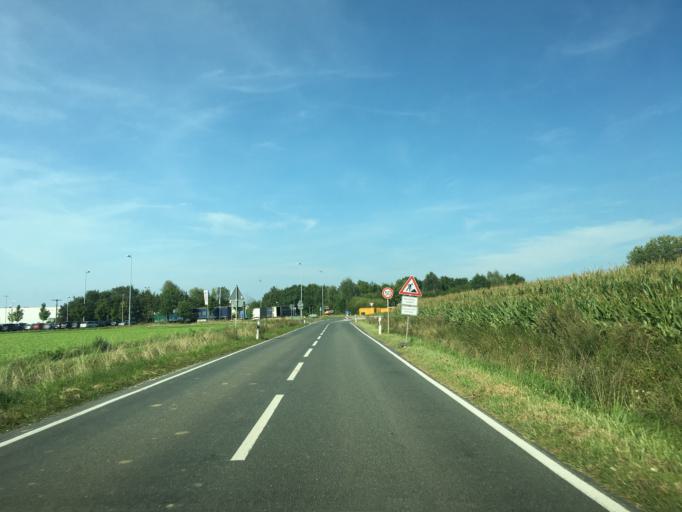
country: DE
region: North Rhine-Westphalia
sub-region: Regierungsbezirk Munster
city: Altenberge
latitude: 52.0295
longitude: 7.4510
